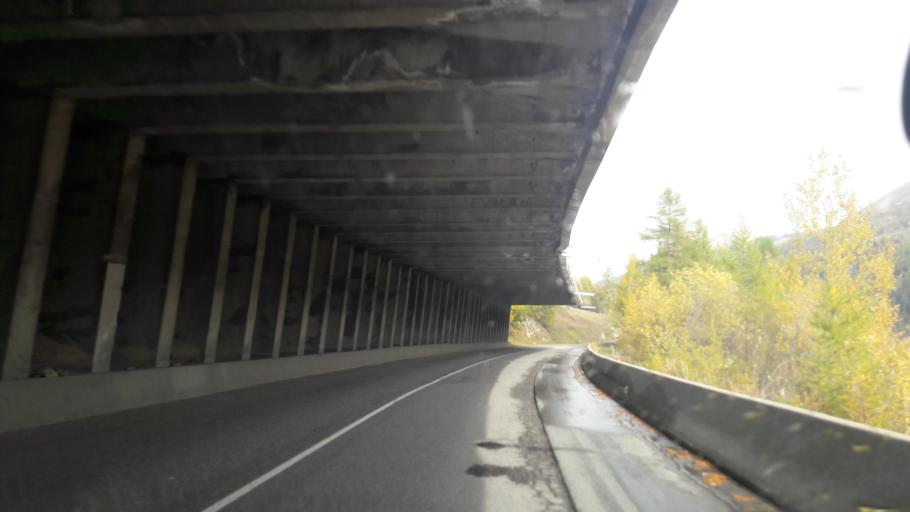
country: FR
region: Rhone-Alpes
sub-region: Departement de la Savoie
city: Tignes
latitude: 45.4900
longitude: 6.9256
